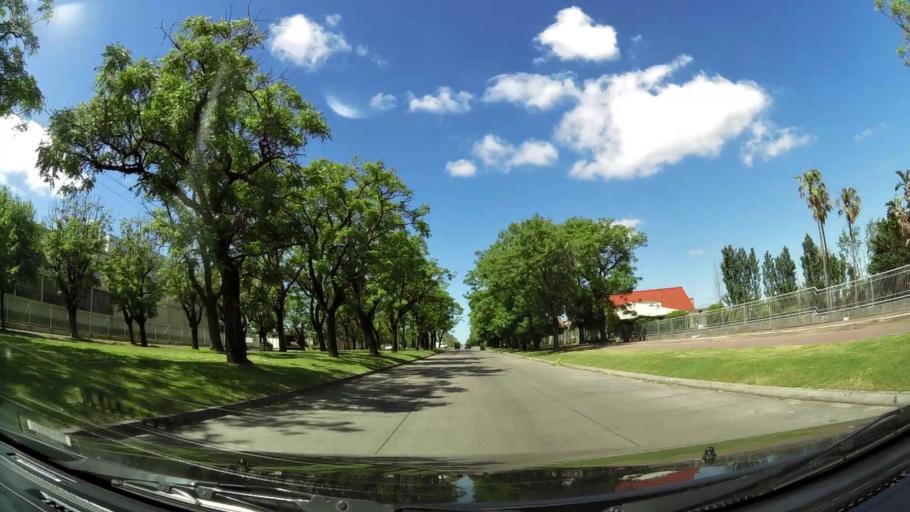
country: UY
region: Montevideo
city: Montevideo
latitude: -34.8514
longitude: -56.1486
